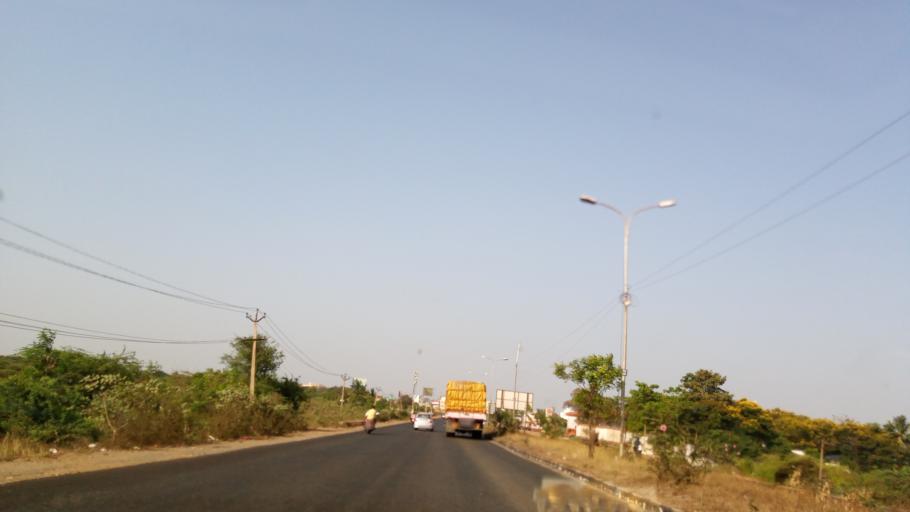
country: IN
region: Tamil Nadu
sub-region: Kancheepuram
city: Sriperumbudur
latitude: 12.9909
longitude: 79.9838
